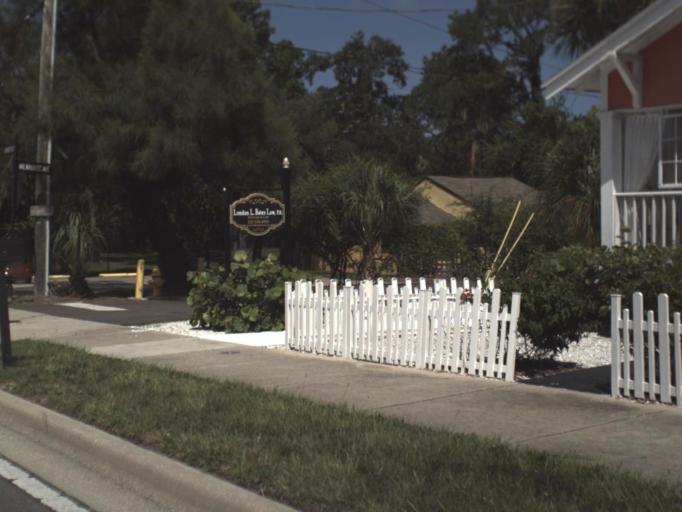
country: US
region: Florida
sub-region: Pinellas County
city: Dunedin
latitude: 28.0159
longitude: -82.7836
